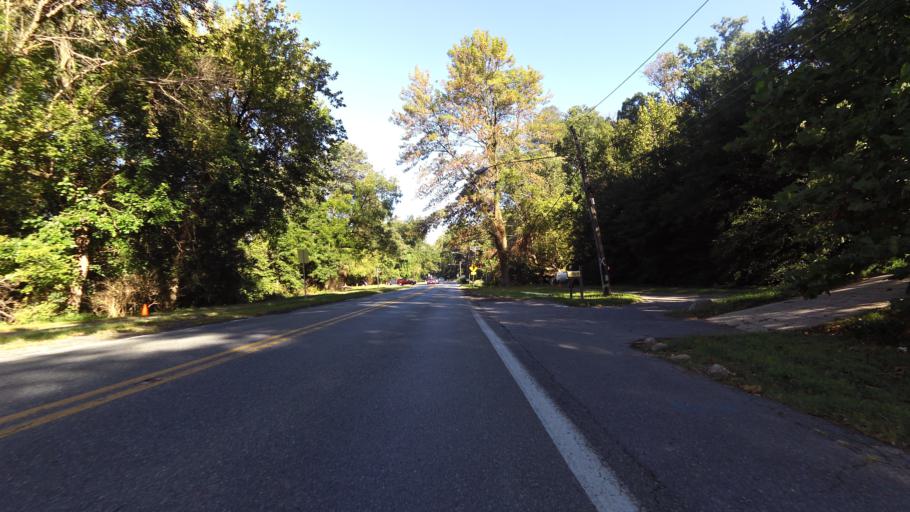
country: US
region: Maryland
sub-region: Montgomery County
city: Brookmont
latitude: 38.9575
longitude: -77.1301
